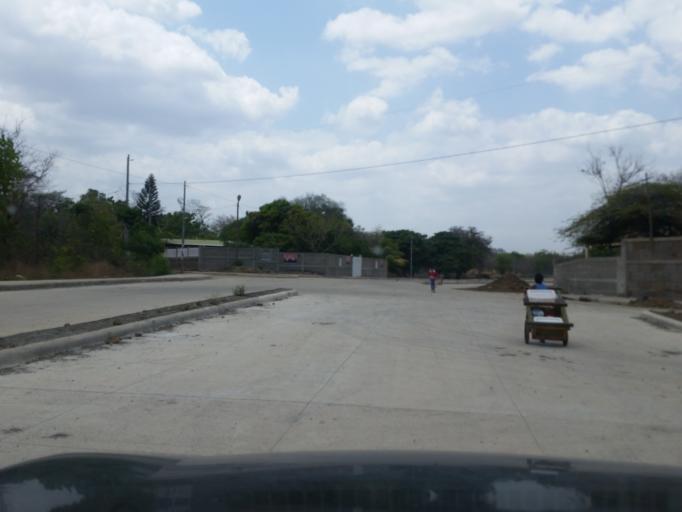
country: NI
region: Managua
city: Managua
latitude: 12.1330
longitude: -86.1843
